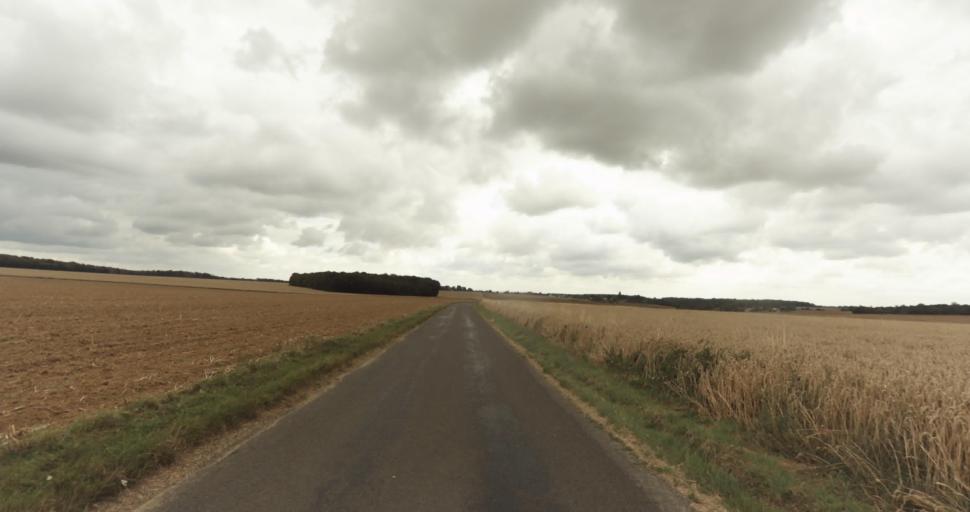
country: FR
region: Haute-Normandie
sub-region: Departement de l'Eure
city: Menilles
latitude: 49.0201
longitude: 1.2882
